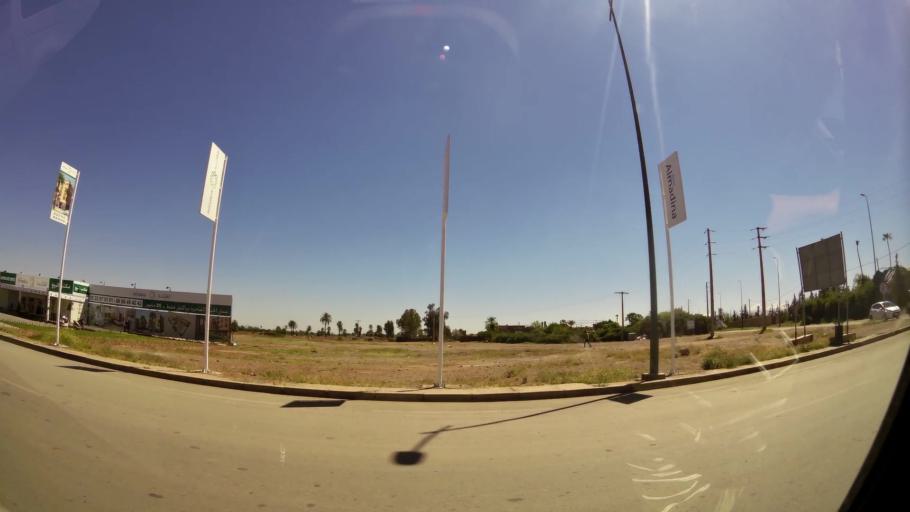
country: MA
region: Marrakech-Tensift-Al Haouz
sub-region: Marrakech
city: Marrakesh
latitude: 31.5749
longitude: -7.9813
